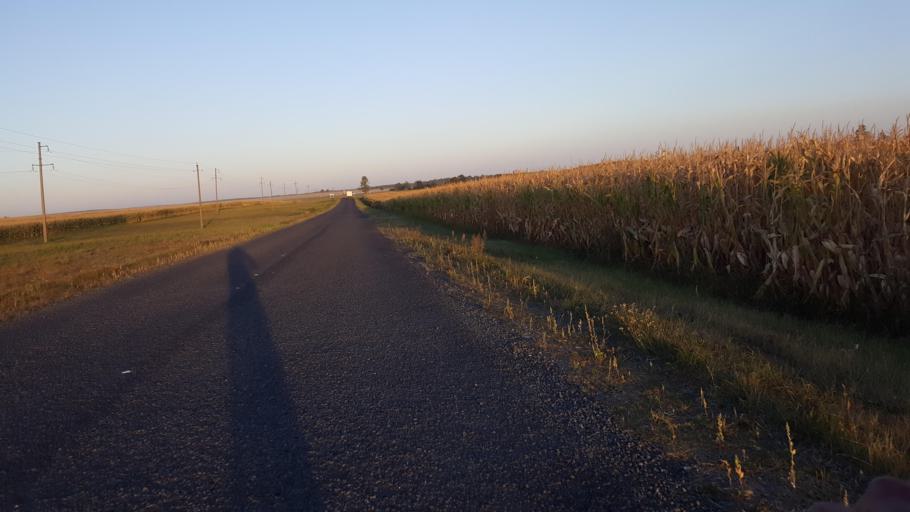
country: BY
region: Brest
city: Charnawchytsy
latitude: 52.2907
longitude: 23.5688
